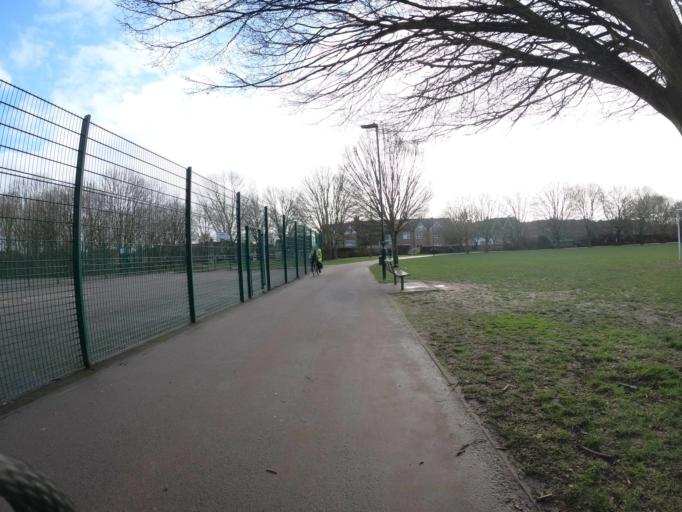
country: GB
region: England
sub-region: Greater London
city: Acton
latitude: 51.5036
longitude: -0.2613
